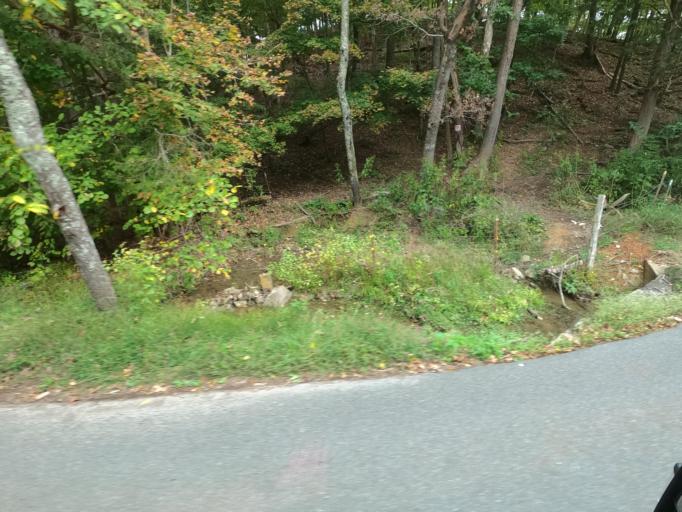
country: US
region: Tennessee
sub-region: Washington County
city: Jonesborough
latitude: 36.2664
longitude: -82.5364
